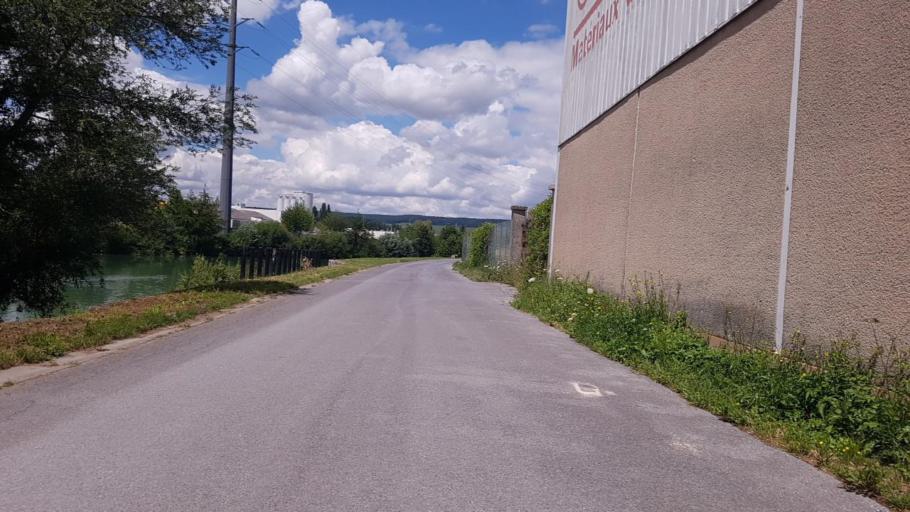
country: FR
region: Champagne-Ardenne
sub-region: Departement de la Marne
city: Magenta
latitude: 49.0512
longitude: 3.9631
